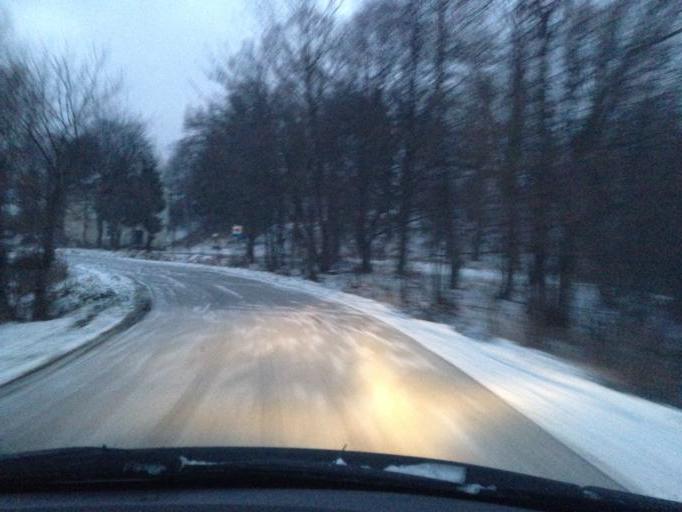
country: PL
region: Subcarpathian Voivodeship
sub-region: Powiat jasielski
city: Krempna
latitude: 49.5265
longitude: 21.5544
